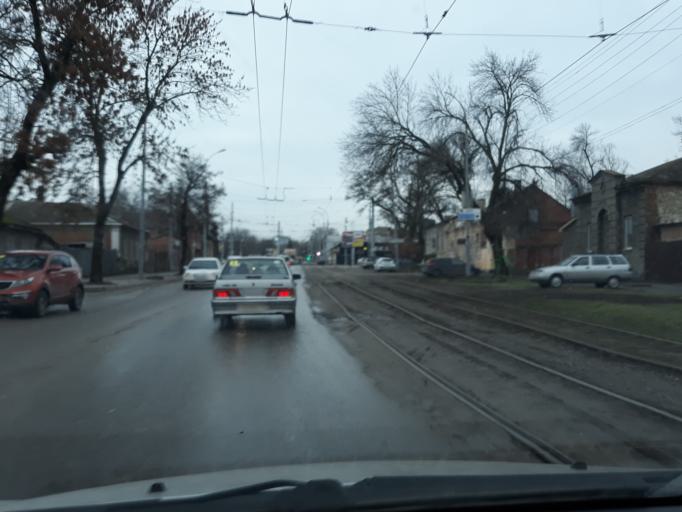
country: RU
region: Rostov
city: Taganrog
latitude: 47.2242
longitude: 38.9181
